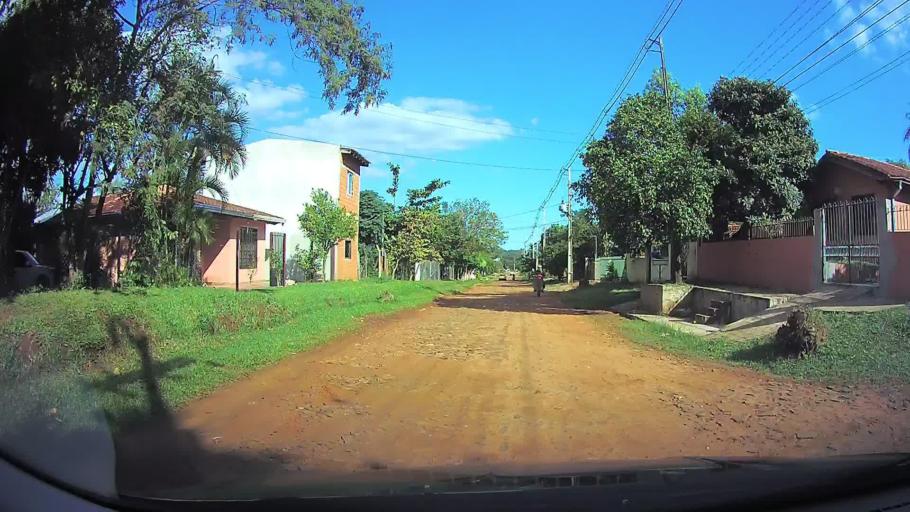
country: PY
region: Central
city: Limpio
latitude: -25.2528
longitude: -57.4749
